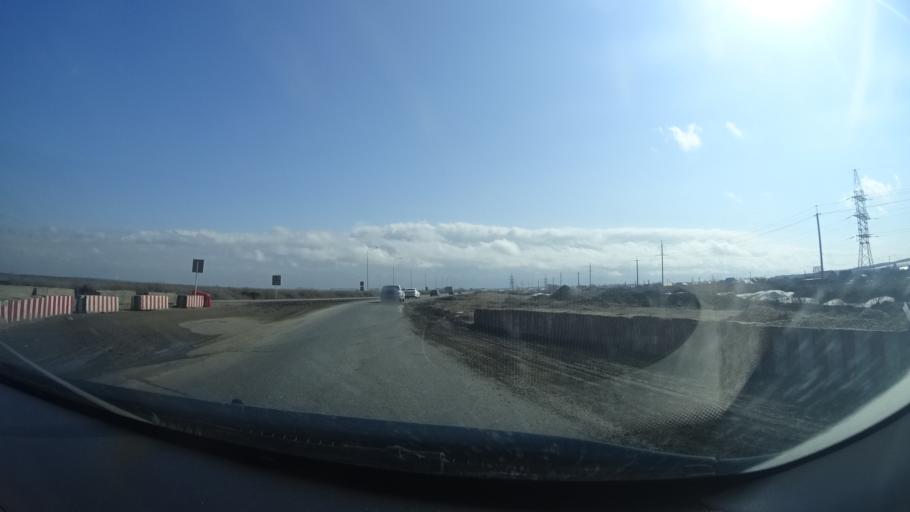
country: RU
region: Bashkortostan
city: Mikhaylovka
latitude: 54.8776
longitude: 55.7172
